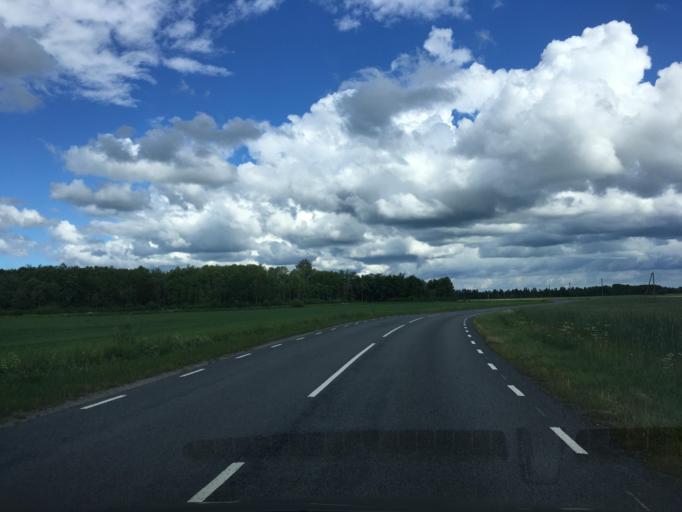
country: EE
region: Paernumaa
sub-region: Halinga vald
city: Parnu-Jaagupi
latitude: 58.6216
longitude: 24.4399
